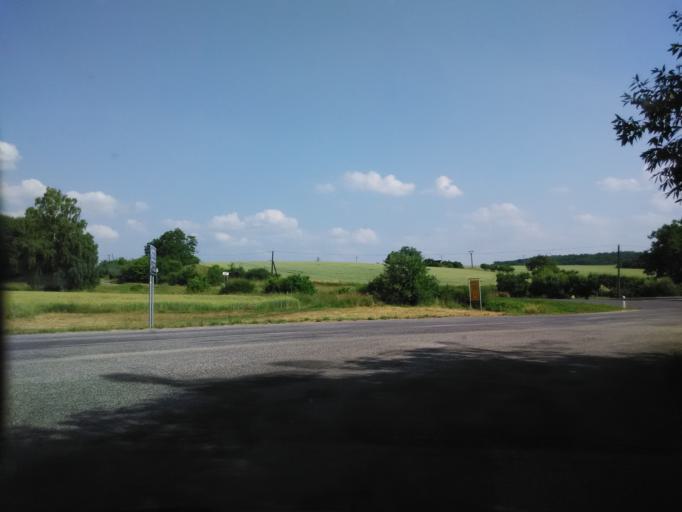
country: SK
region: Nitriansky
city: Levice
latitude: 48.2641
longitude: 18.7094
